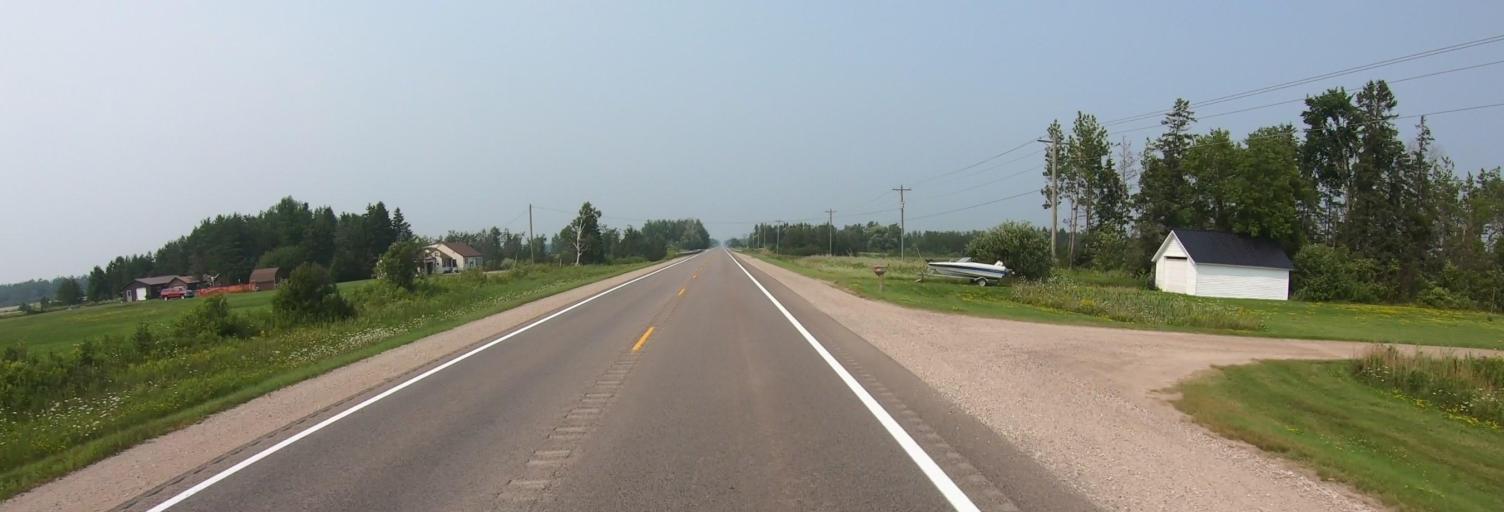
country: US
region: Michigan
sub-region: Chippewa County
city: Sault Ste. Marie
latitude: 46.1746
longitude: -84.3632
